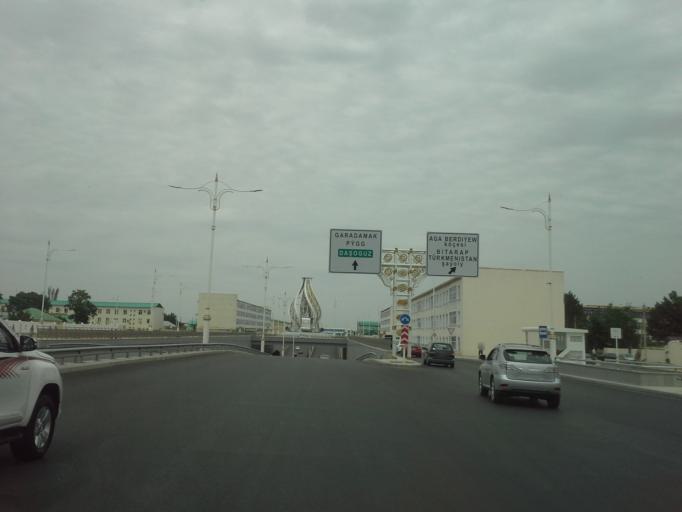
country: TM
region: Ahal
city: Ashgabat
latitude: 37.9424
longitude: 58.4028
